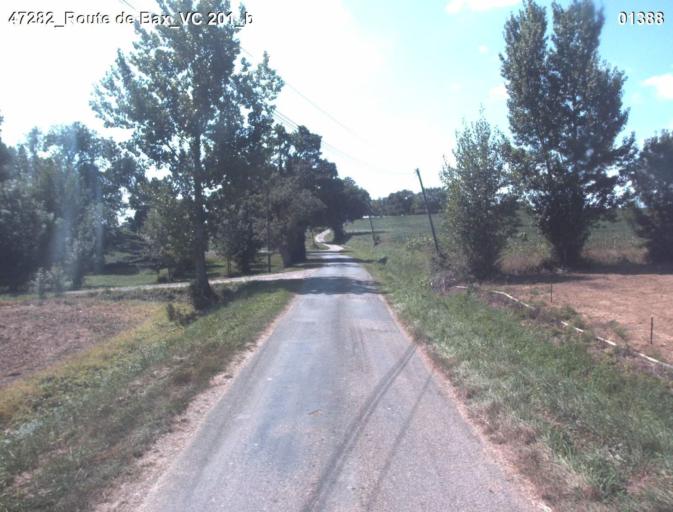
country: FR
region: Aquitaine
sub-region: Departement du Lot-et-Garonne
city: Laplume
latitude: 44.0803
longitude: 0.4961
